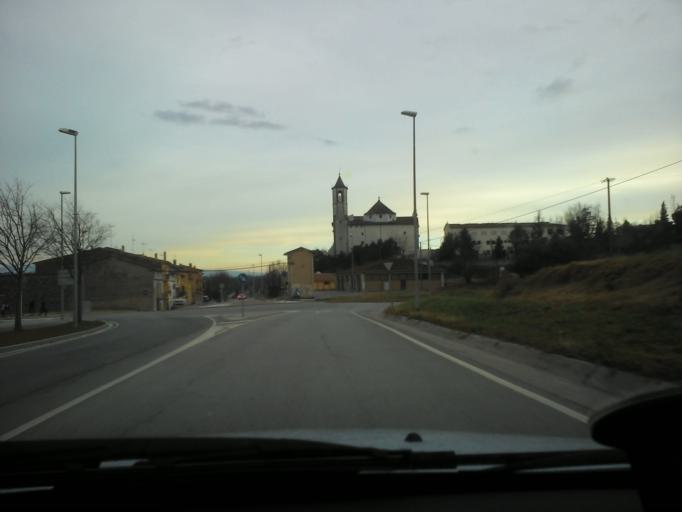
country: ES
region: Catalonia
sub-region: Provincia de Barcelona
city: Santa Cecilia de Voltrega
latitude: 42.0060
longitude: 2.2411
